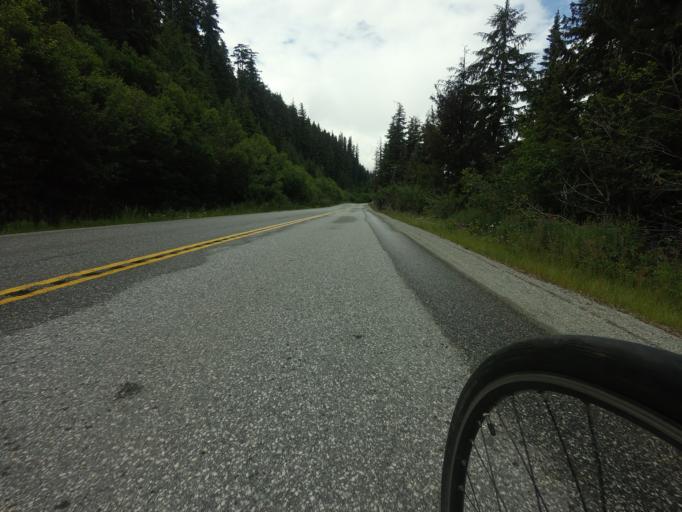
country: CA
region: British Columbia
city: Lillooet
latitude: 50.3991
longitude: -122.3153
